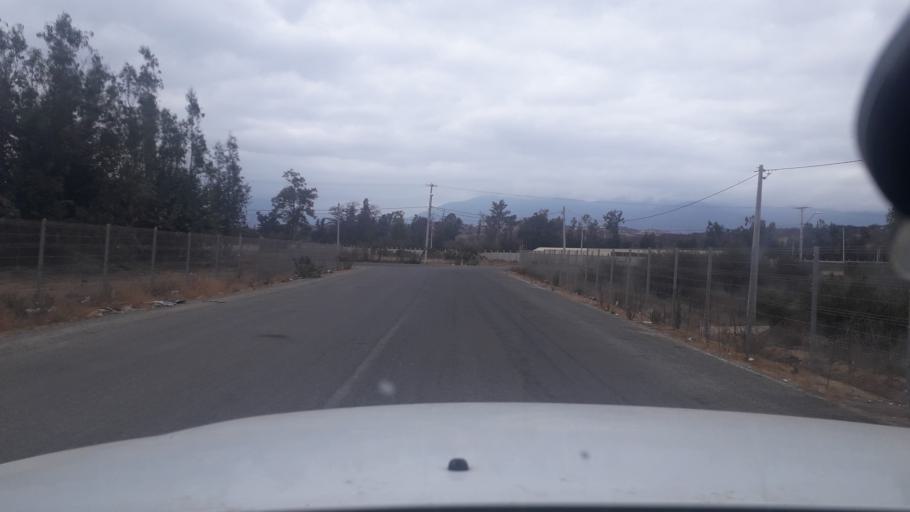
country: CL
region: Valparaiso
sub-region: Provincia de Marga Marga
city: Limache
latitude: -33.0239
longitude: -71.2758
